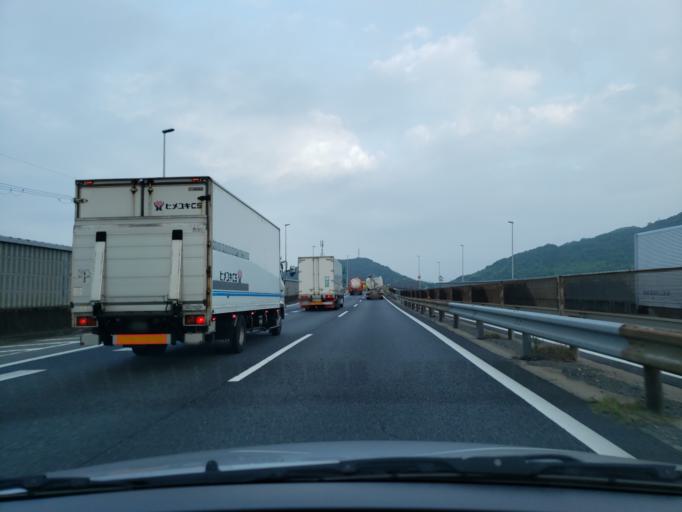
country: JP
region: Hyogo
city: Tatsunocho-tominaga
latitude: 34.8476
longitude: 134.5888
